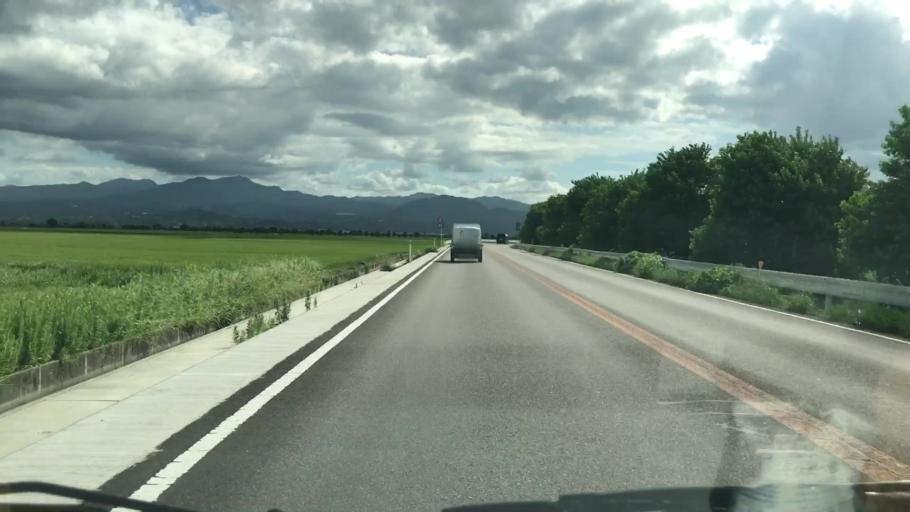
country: JP
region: Saga Prefecture
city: Kashima
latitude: 33.1397
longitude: 130.1435
